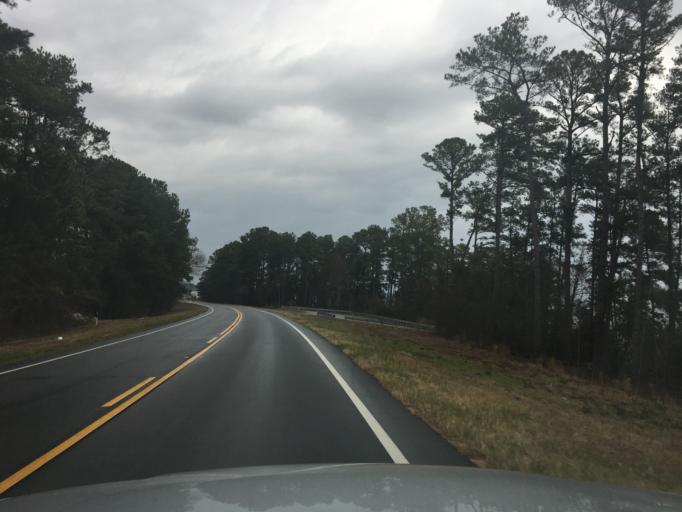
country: US
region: Georgia
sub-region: Columbia County
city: Appling
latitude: 33.6836
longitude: -82.3337
